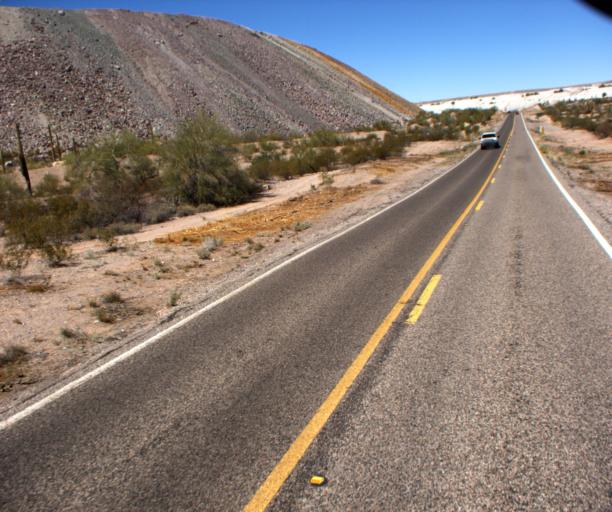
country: US
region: Arizona
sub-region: Pima County
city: Ajo
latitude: 32.3632
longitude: -112.8359
